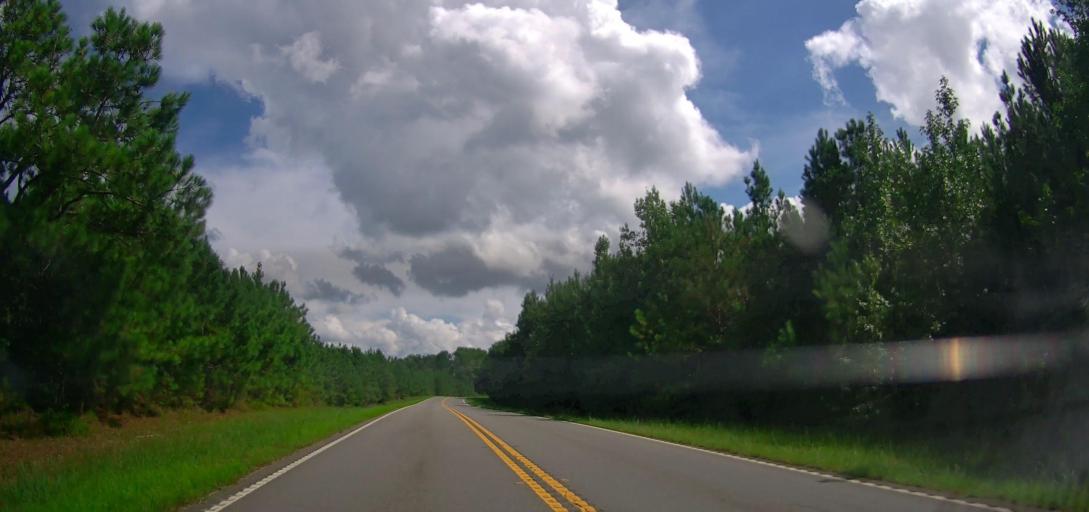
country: US
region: Georgia
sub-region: Talbot County
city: Talbotton
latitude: 32.6575
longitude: -84.5094
